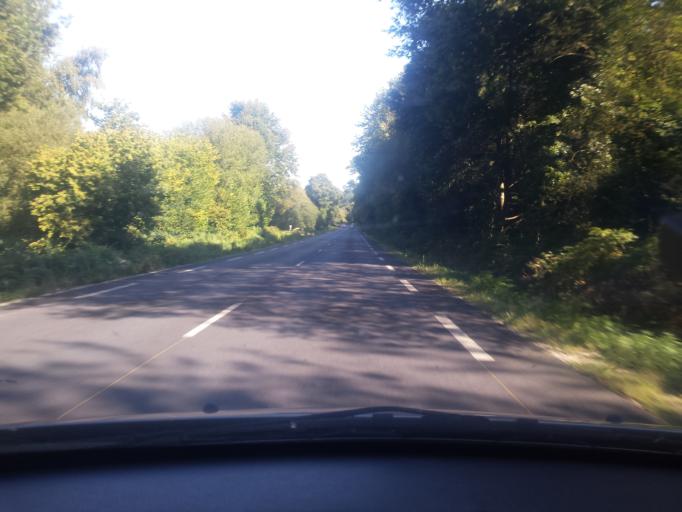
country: FR
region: Brittany
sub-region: Departement du Morbihan
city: Malguenac
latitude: 48.0979
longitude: -3.0528
